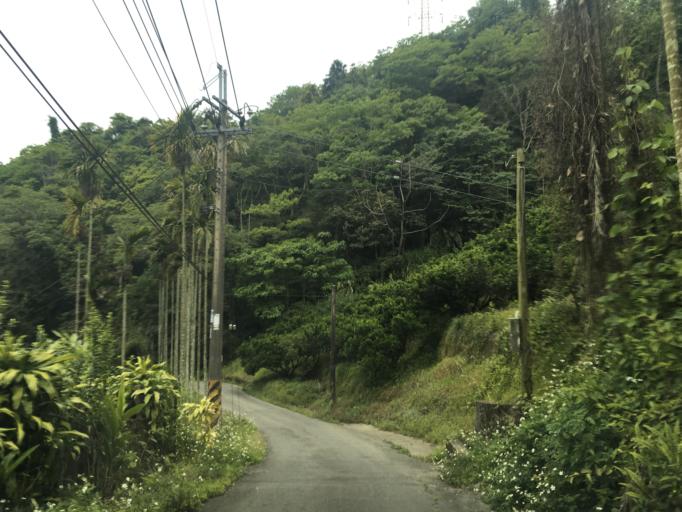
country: TW
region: Taiwan
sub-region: Taichung City
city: Taichung
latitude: 24.1540
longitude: 120.8264
